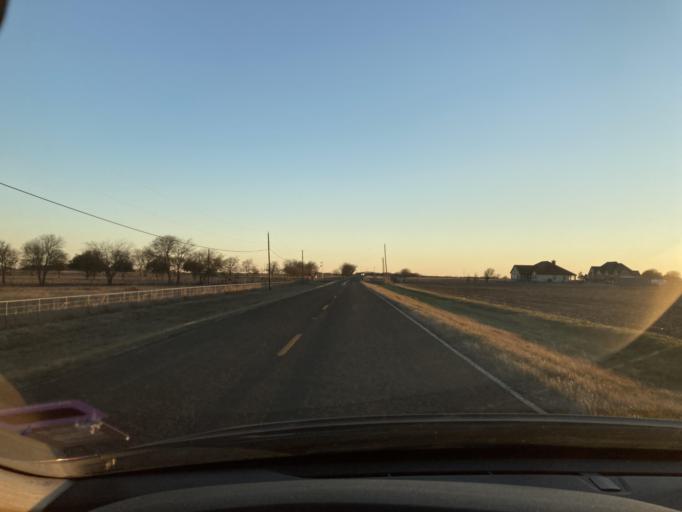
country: US
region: Texas
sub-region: Ellis County
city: Waxahachie
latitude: 32.3314
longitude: -96.8754
